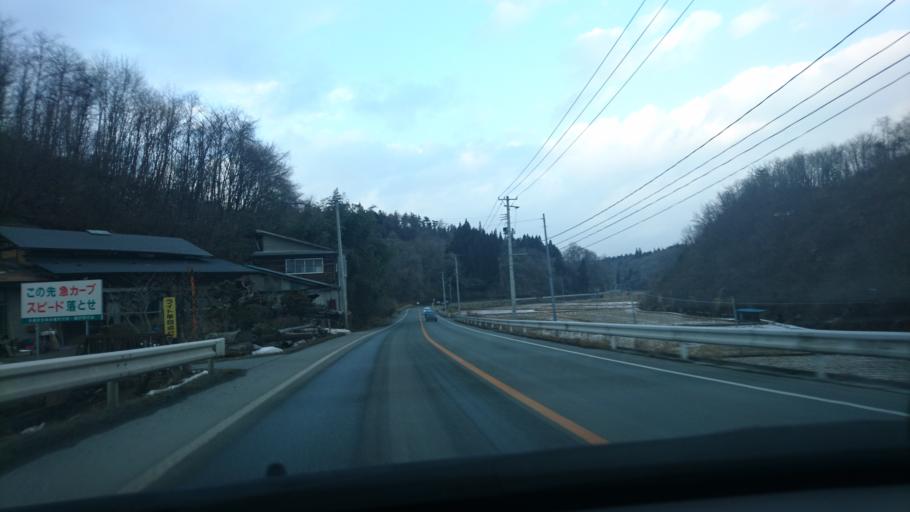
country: JP
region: Iwate
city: Ichinoseki
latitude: 38.9805
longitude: 141.3308
